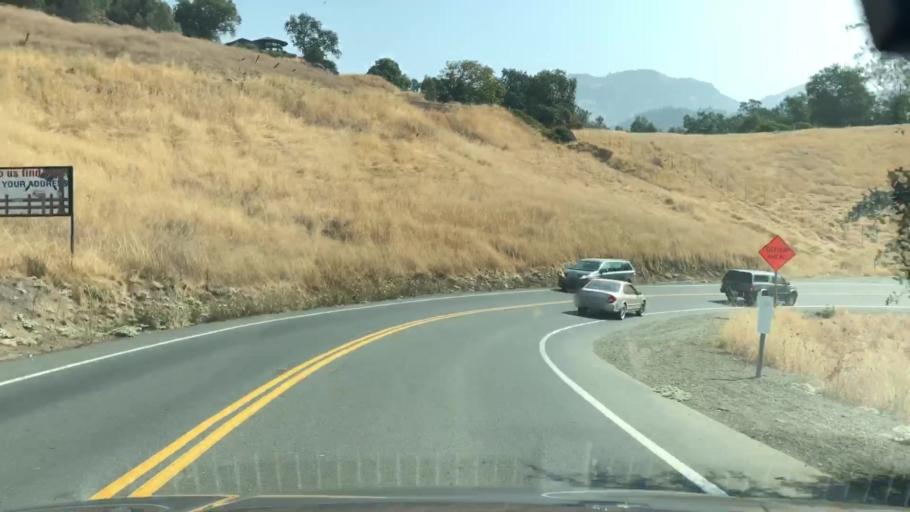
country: US
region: California
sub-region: Napa County
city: Calistoga
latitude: 38.6068
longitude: -122.5975
